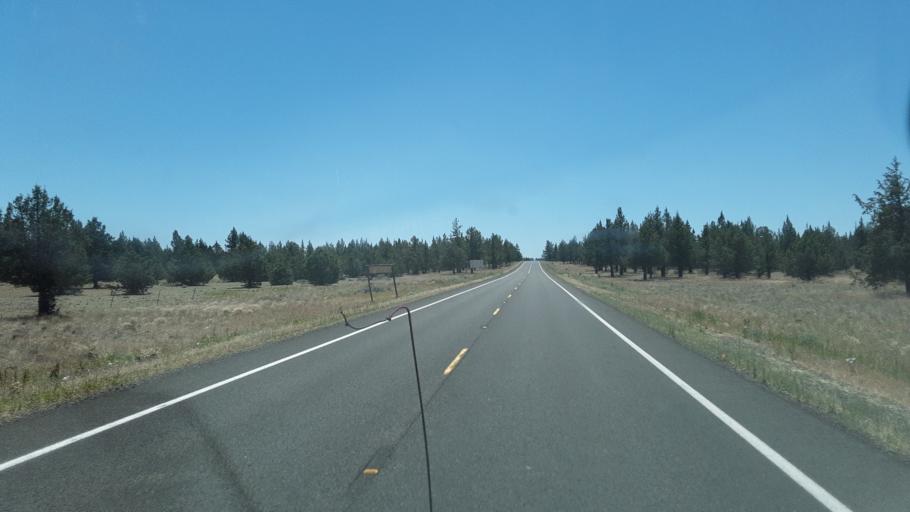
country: US
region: California
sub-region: Siskiyou County
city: Tulelake
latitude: 41.6686
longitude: -121.2557
